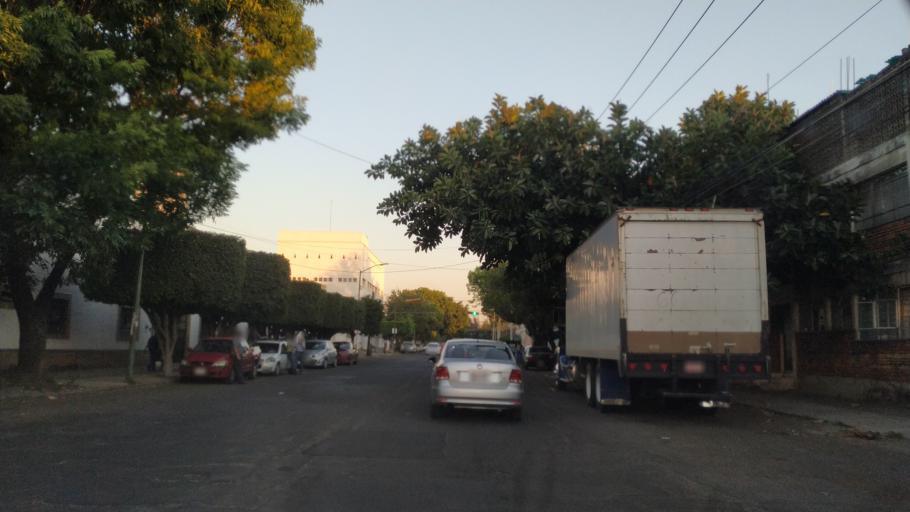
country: MX
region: Jalisco
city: Tlaquepaque
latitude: 20.6568
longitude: -103.3316
